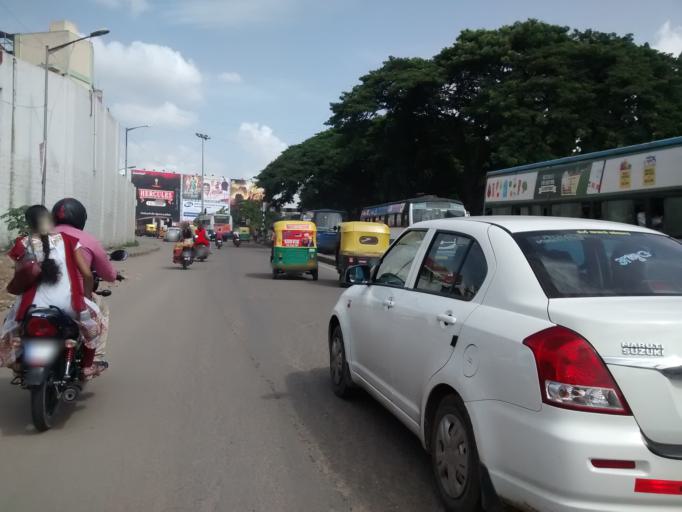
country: IN
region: Karnataka
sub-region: Bangalore Urban
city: Bangalore
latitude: 12.9810
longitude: 77.5705
